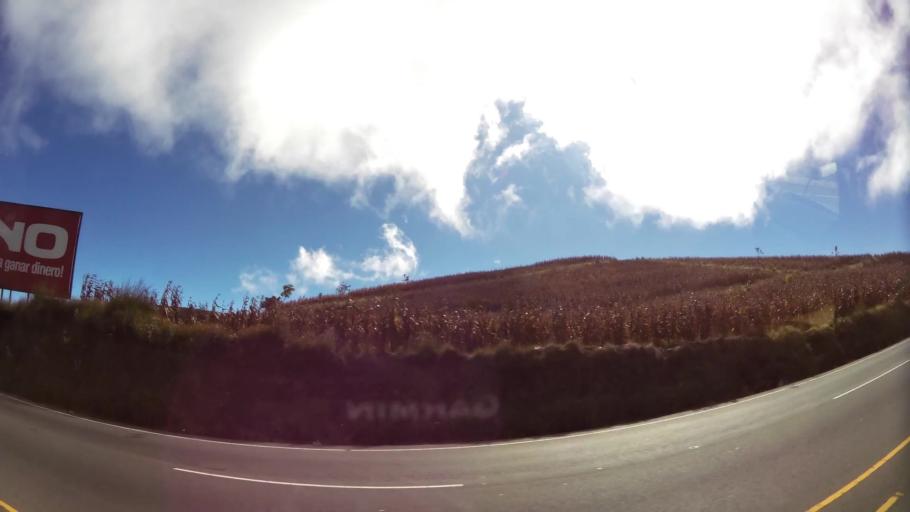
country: GT
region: Solola
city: Santa Catarina Ixtahuacan
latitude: 14.8414
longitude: -91.3628
